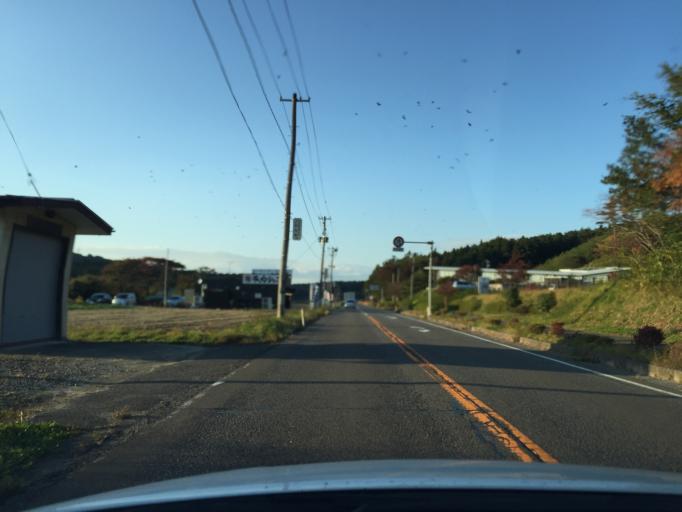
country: JP
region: Fukushima
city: Ishikawa
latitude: 37.2579
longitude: 140.5581
